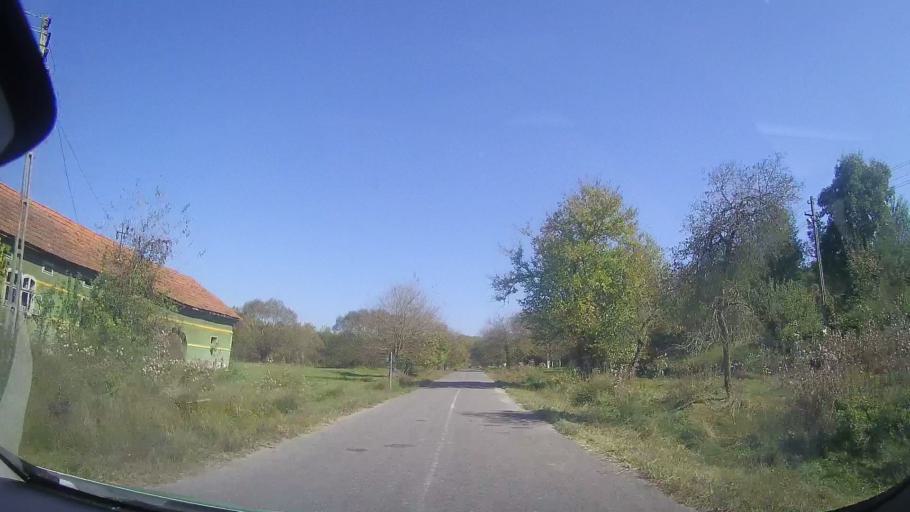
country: RO
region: Timis
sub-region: Comuna Bara
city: Bara
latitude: 45.8945
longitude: 21.9223
